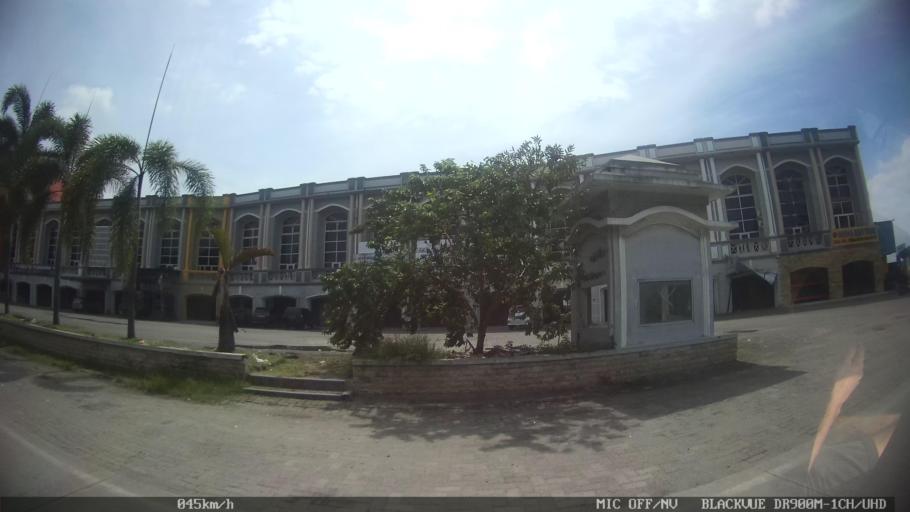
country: ID
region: North Sumatra
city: Medan
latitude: 3.6334
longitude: 98.7080
